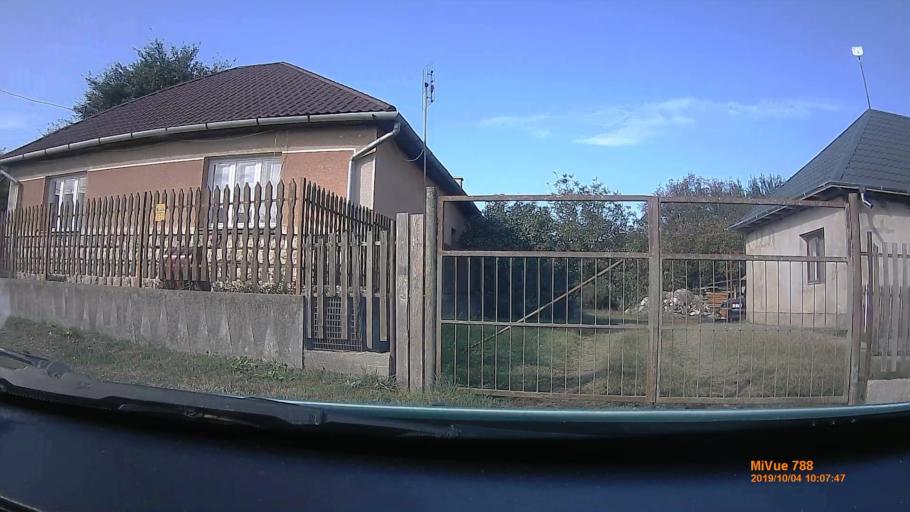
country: HU
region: Szabolcs-Szatmar-Bereg
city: Nyiregyhaza
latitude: 47.9439
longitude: 21.6838
